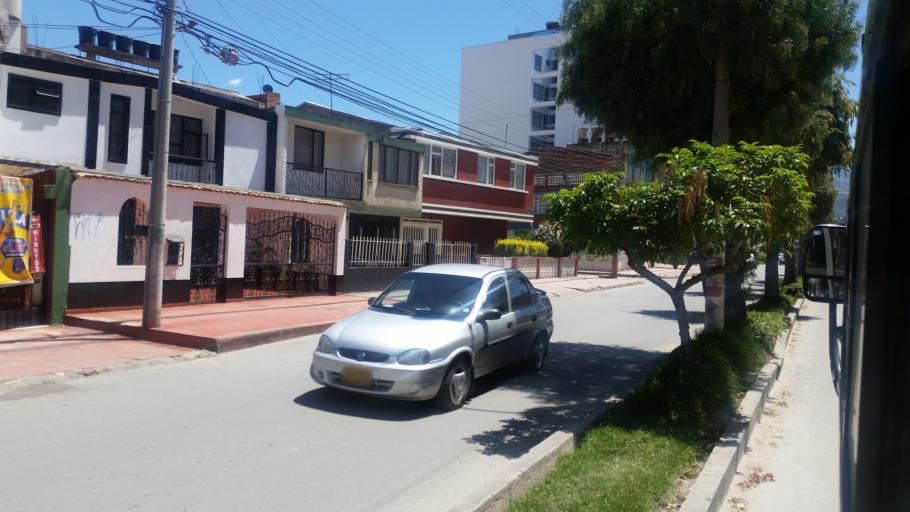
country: CO
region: Boyaca
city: Sogamoso
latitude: 5.7220
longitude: -72.9301
